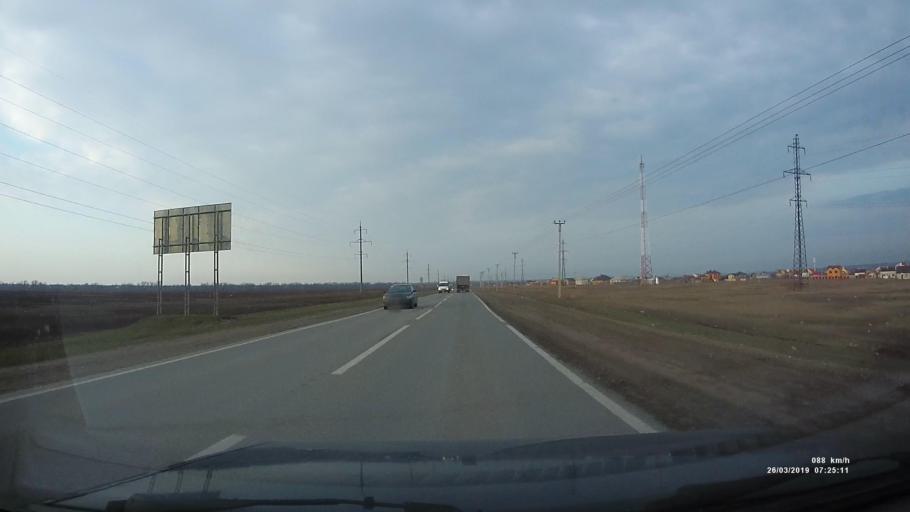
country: RU
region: Rostov
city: Taganrog
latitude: 47.2734
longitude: 38.8526
